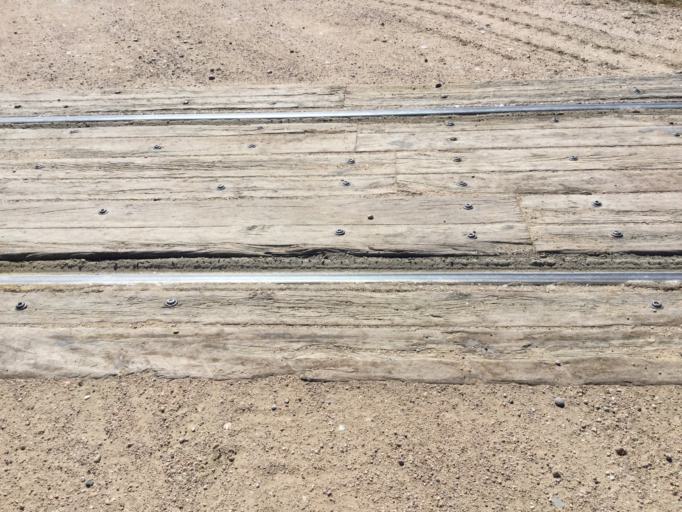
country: US
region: Kansas
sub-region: Grant County
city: Ulysses
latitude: 37.5817
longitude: -101.2722
